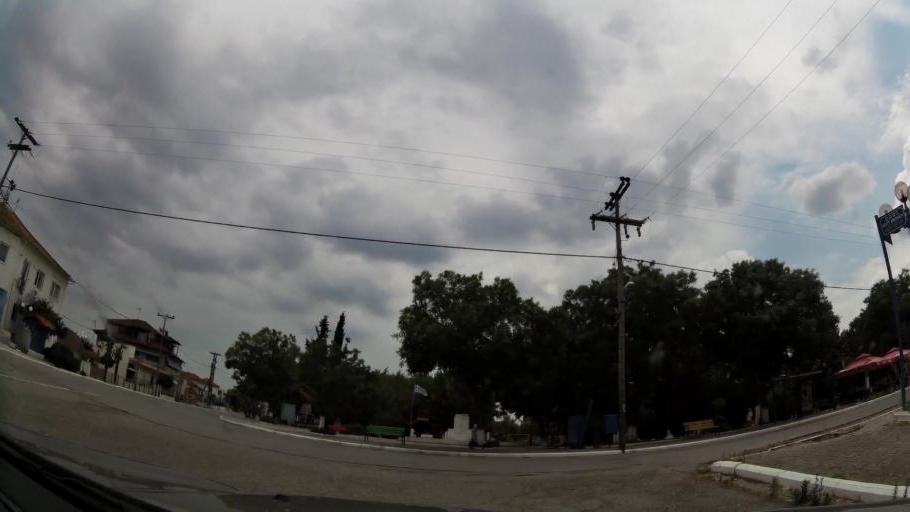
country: GR
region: Central Macedonia
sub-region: Nomos Pierias
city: Kallithea
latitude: 40.2767
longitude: 22.5784
